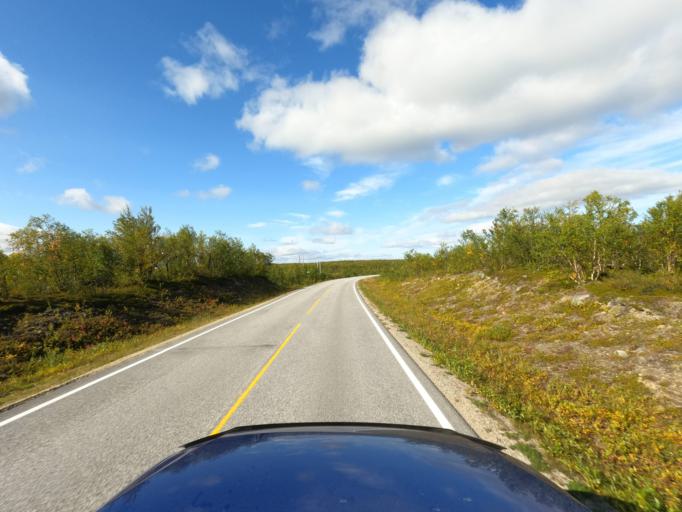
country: NO
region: Finnmark Fylke
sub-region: Karasjok
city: Karasjohka
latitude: 69.6103
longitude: 25.3108
